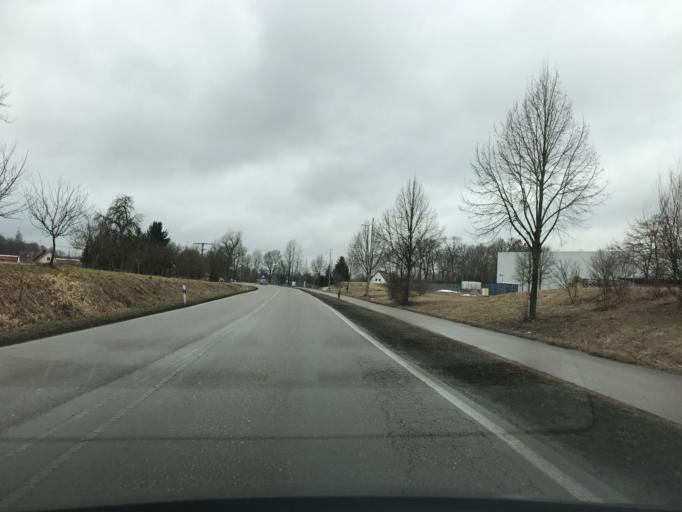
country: DE
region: Baden-Wuerttemberg
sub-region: Tuebingen Region
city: Laupheim
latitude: 48.2428
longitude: 9.8716
